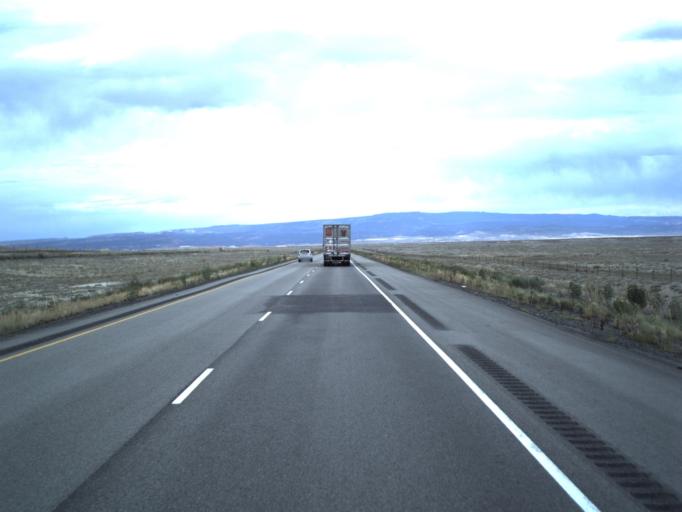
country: US
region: Utah
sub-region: Grand County
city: Moab
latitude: 38.9340
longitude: -109.4552
